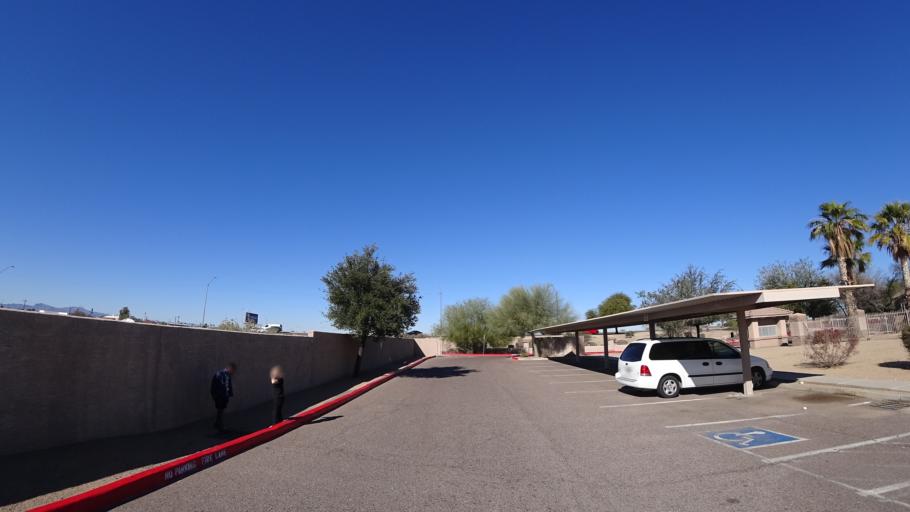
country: US
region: Arizona
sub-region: Maricopa County
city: Avondale
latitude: 33.4341
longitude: -112.3375
